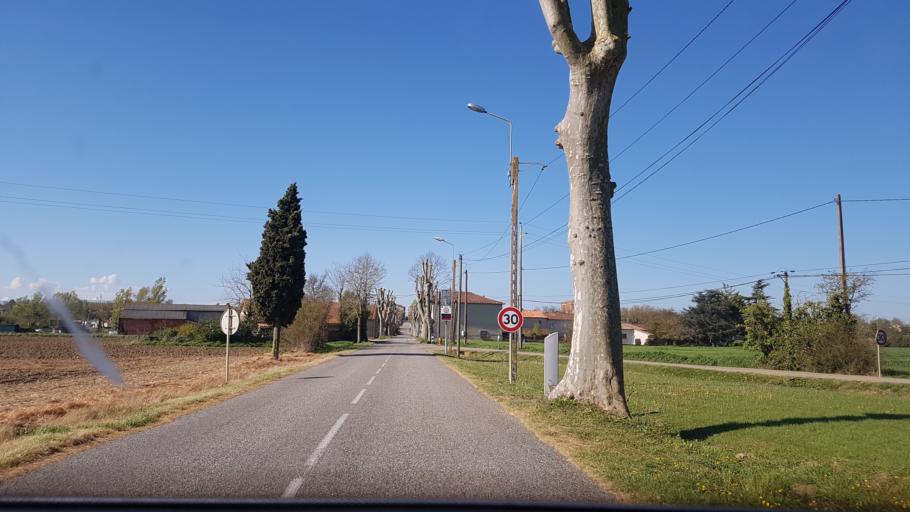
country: FR
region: Midi-Pyrenees
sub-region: Departement de l'Ariege
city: Mazeres
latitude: 43.2567
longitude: 1.6847
